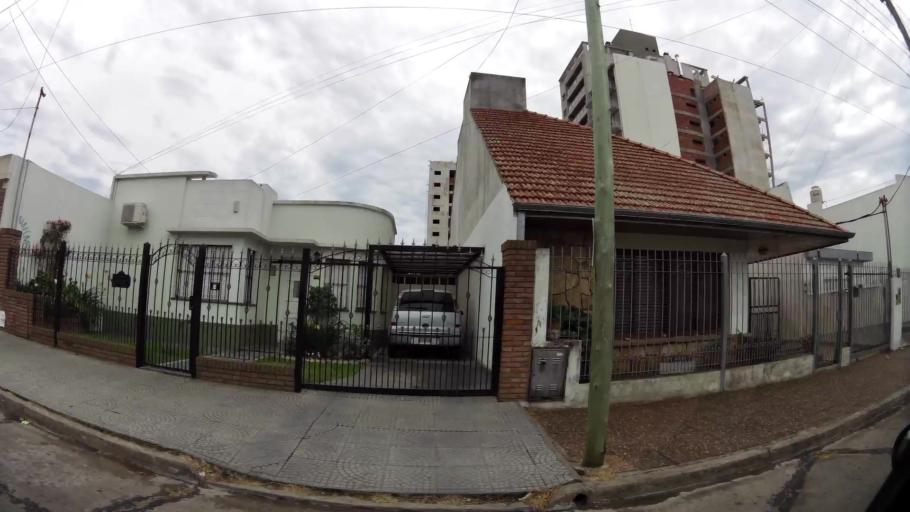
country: AR
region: Buenos Aires
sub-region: Partido de Quilmes
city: Quilmes
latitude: -34.7570
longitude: -58.2138
